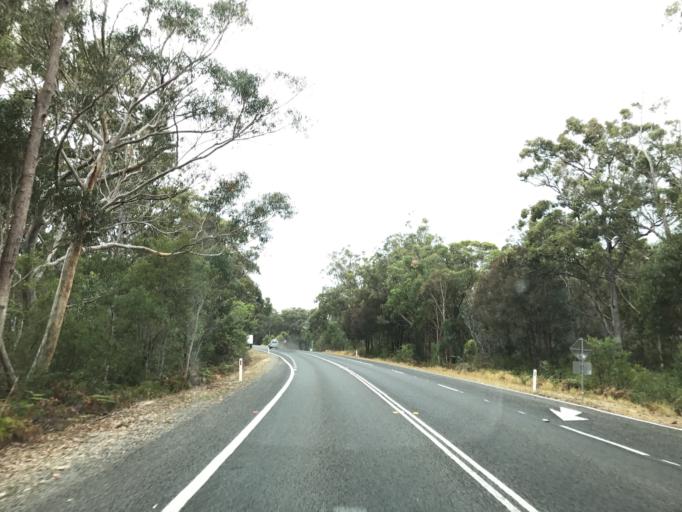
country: AU
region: Queensland
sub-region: Redland
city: Victoria Point
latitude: -27.4414
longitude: 153.4840
